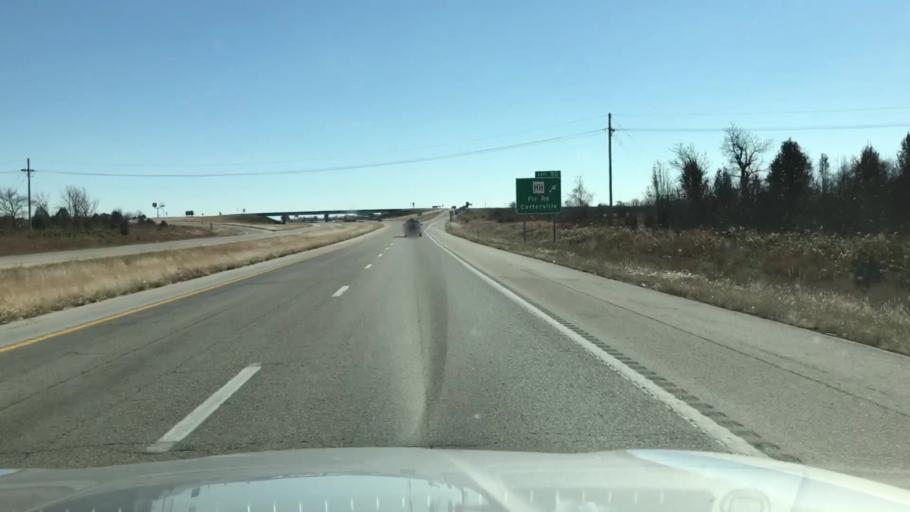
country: US
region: Missouri
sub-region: Jasper County
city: Carthage
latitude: 37.1448
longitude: -94.3262
